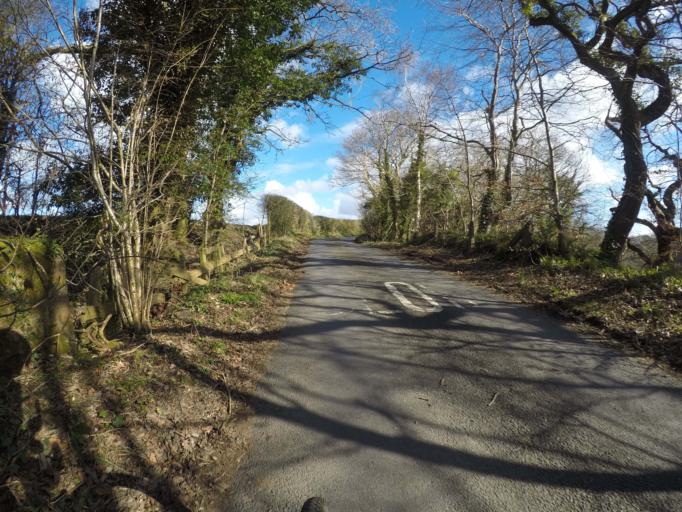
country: GB
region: Scotland
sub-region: North Ayrshire
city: Irvine
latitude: 55.6644
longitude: -4.6506
